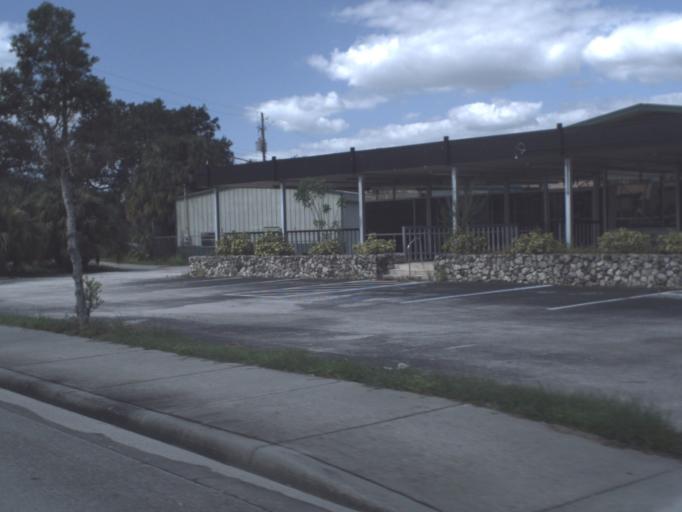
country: US
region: Florida
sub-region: Collier County
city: Naples
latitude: 26.1369
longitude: -81.7805
